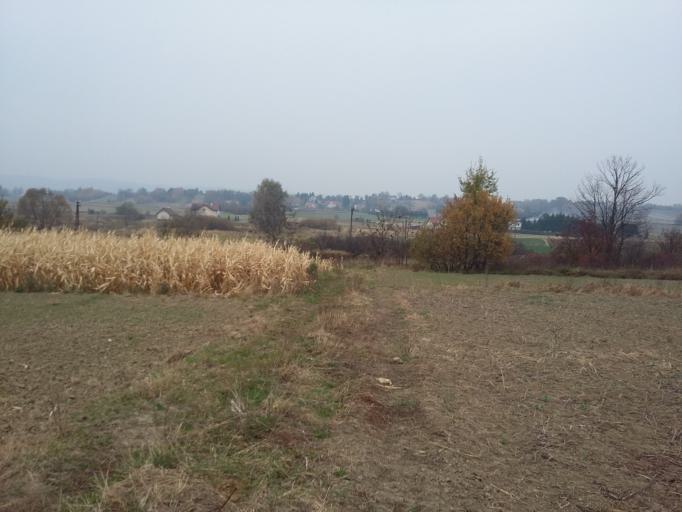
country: PL
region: Subcarpathian Voivodeship
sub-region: Powiat jasielski
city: Tarnowiec
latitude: 49.7347
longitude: 21.5666
